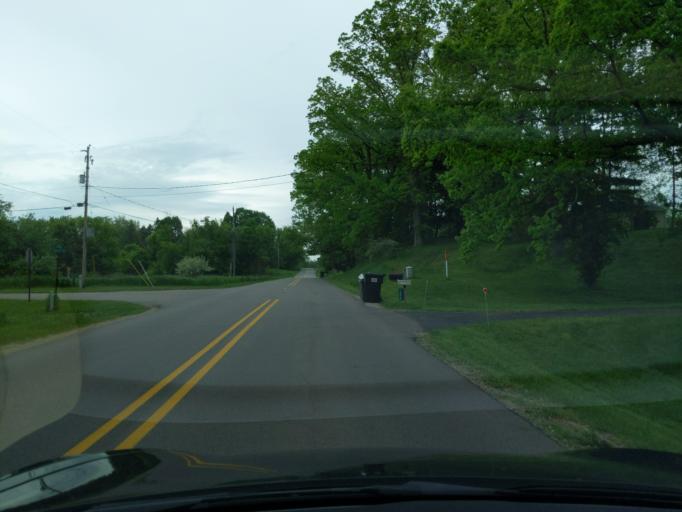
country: US
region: Michigan
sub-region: Jackson County
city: Jackson
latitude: 42.3485
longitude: -84.3486
